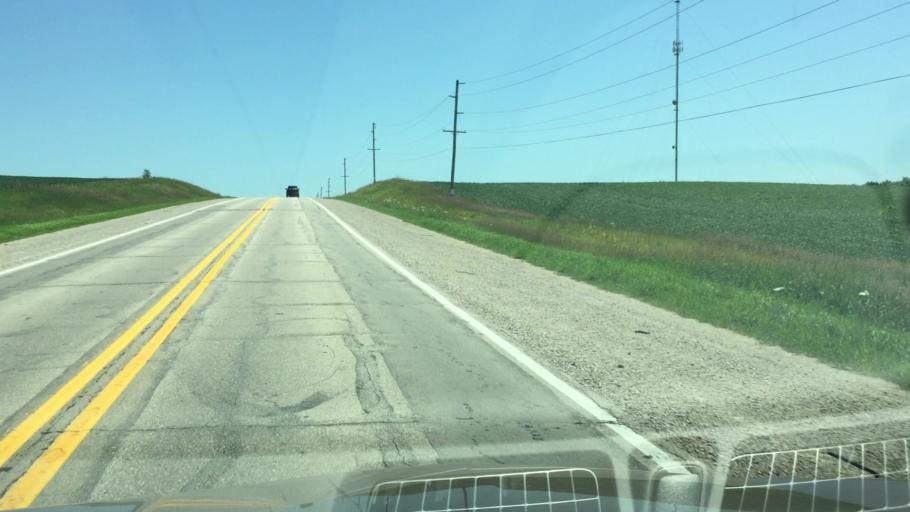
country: US
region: Iowa
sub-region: Cedar County
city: Mechanicsville
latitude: 41.8886
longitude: -91.1781
